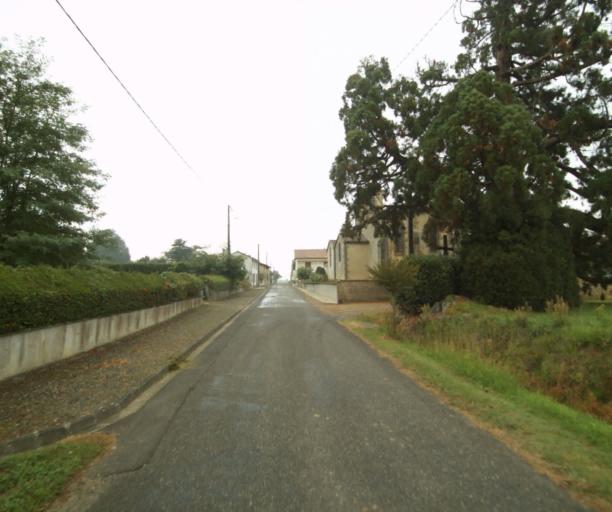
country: FR
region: Midi-Pyrenees
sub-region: Departement du Gers
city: Cazaubon
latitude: 43.9181
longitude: -0.1057
